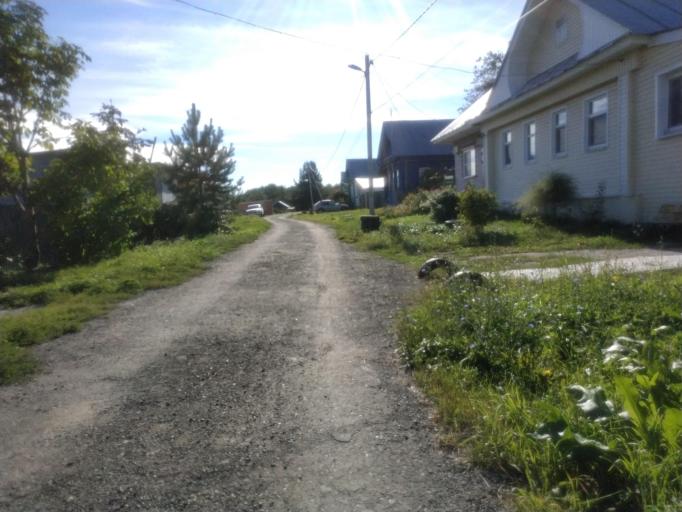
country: RU
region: Chuvashia
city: Novyye Lapsary
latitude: 56.1436
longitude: 47.1482
